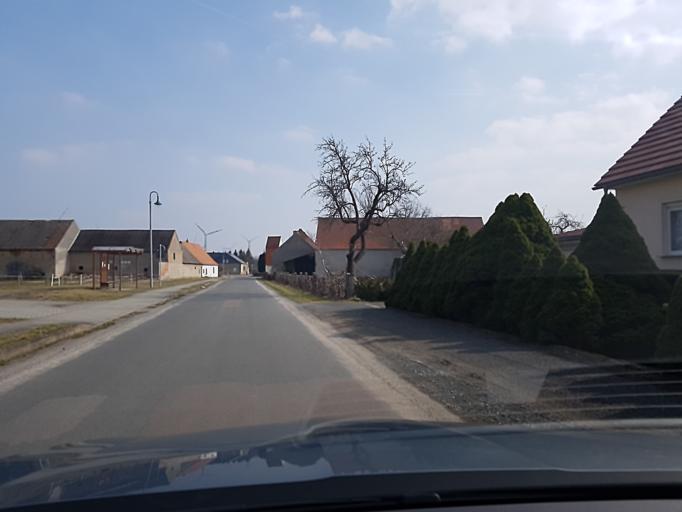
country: DE
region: Brandenburg
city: Falkenberg
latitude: 51.5296
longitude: 13.2952
